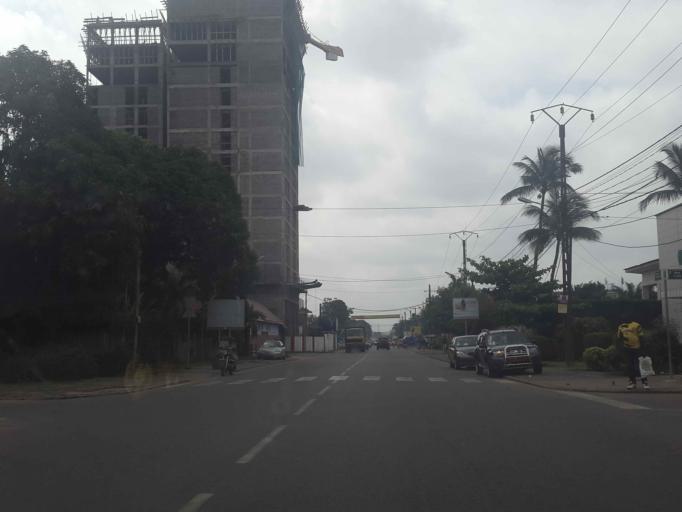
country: CM
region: Littoral
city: Douala
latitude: 4.0272
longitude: 9.6995
